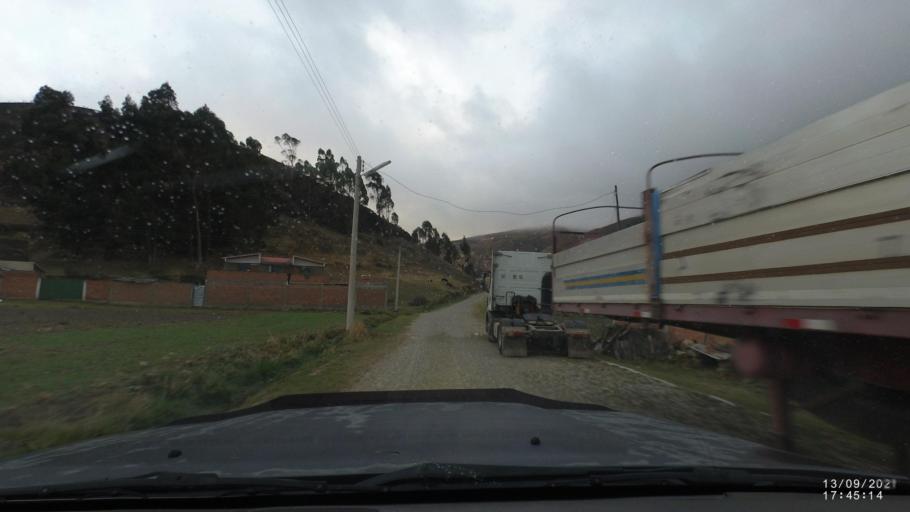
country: BO
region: Cochabamba
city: Colomi
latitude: -17.3766
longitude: -65.8319
